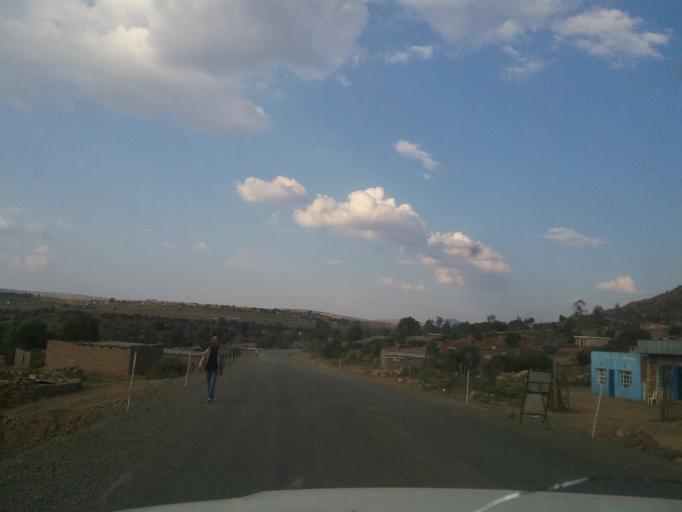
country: LS
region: Quthing
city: Quthing
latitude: -30.3957
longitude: 27.6150
